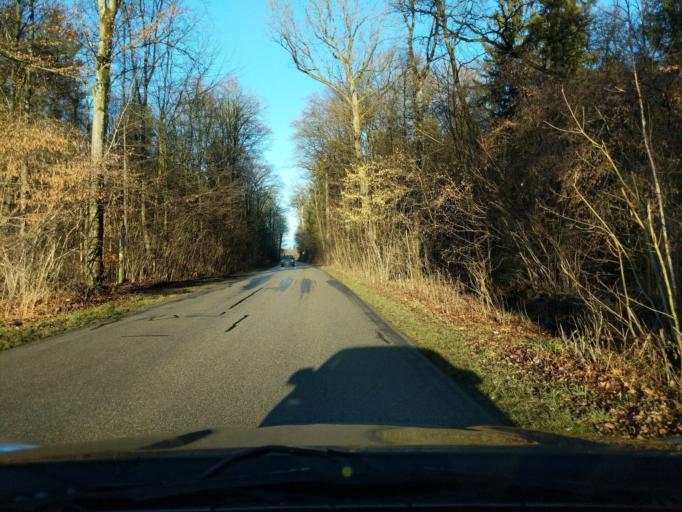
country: DE
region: Bavaria
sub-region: Upper Bavaria
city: Zorneding
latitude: 48.0872
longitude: 11.8506
